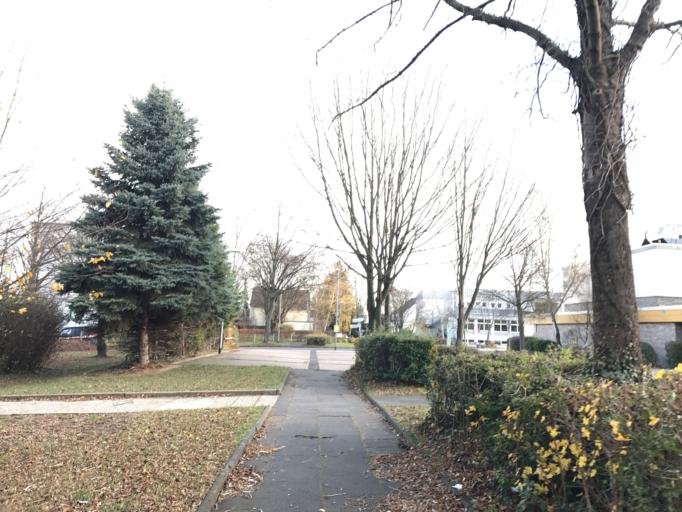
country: DE
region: North Rhine-Westphalia
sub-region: Regierungsbezirk Koln
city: Rheinbach
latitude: 50.6205
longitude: 6.9401
